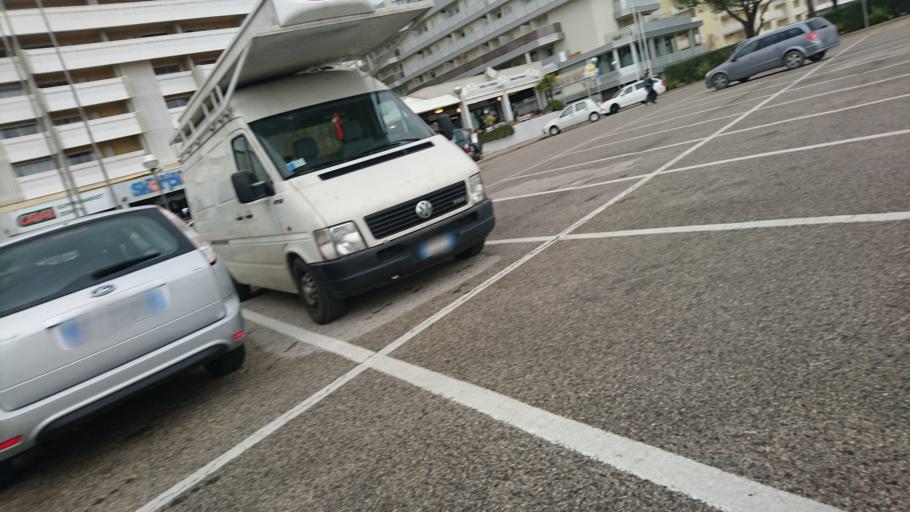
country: IT
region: Veneto
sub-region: Provincia di Venezia
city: Bibione
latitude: 45.6337
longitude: 13.0630
